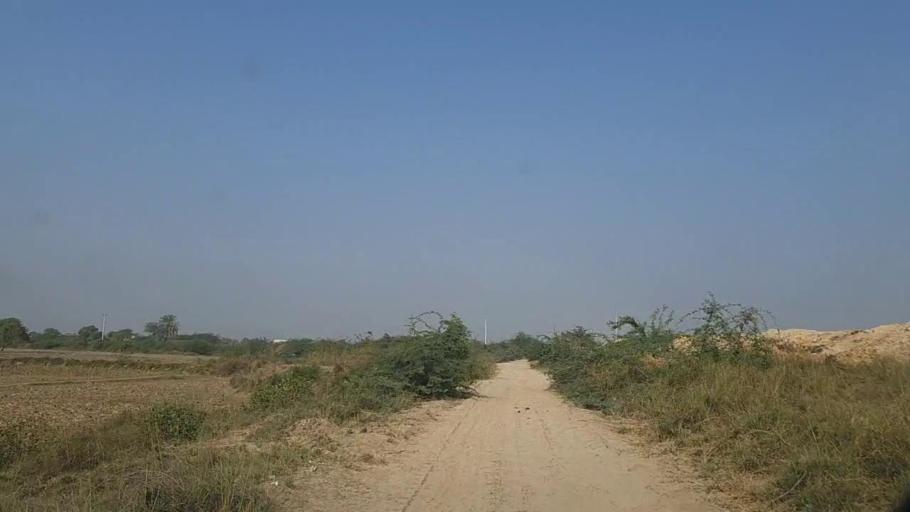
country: PK
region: Sindh
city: Thatta
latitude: 24.6610
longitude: 67.9261
